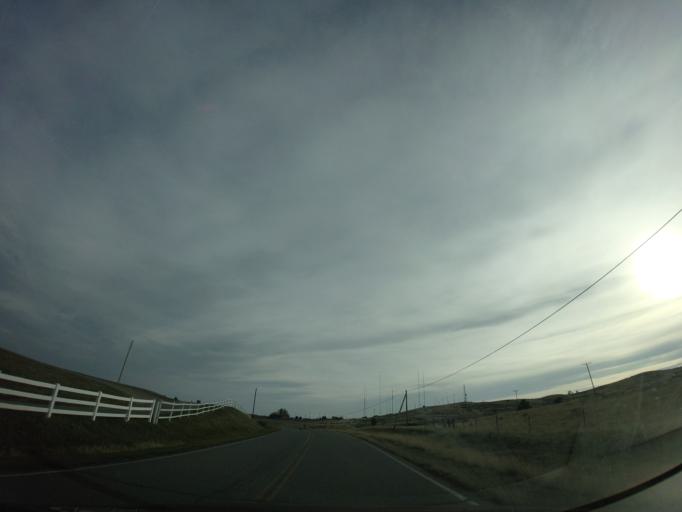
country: US
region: Montana
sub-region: Yellowstone County
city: Billings
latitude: 45.7742
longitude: -108.4612
